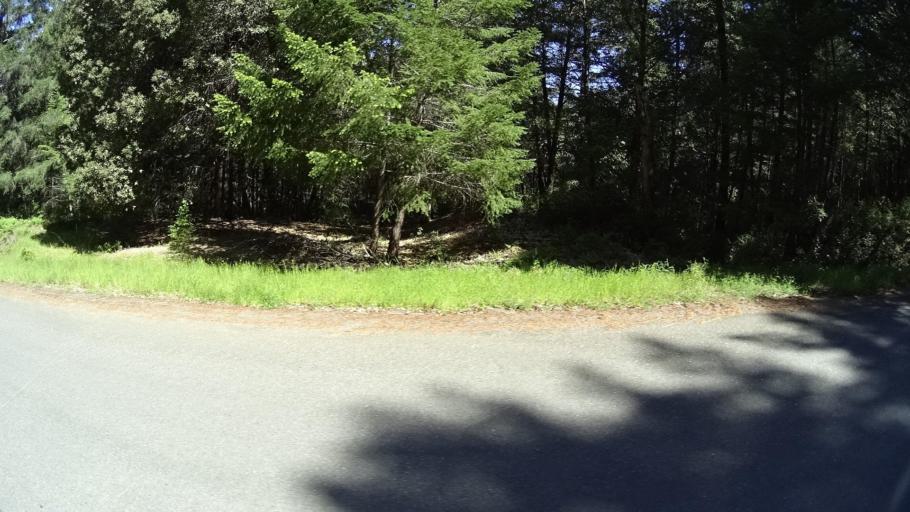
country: US
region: California
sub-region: Humboldt County
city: Redway
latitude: 40.1351
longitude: -123.9898
